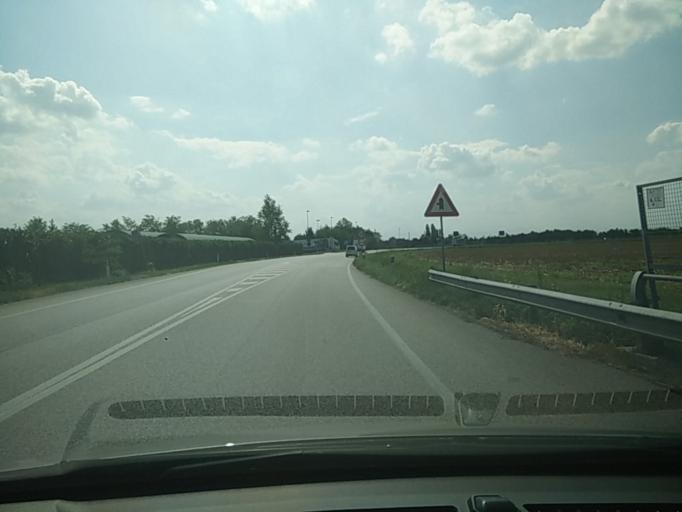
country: IT
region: Veneto
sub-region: Provincia di Treviso
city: Porcellengo
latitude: 45.7188
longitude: 12.1324
